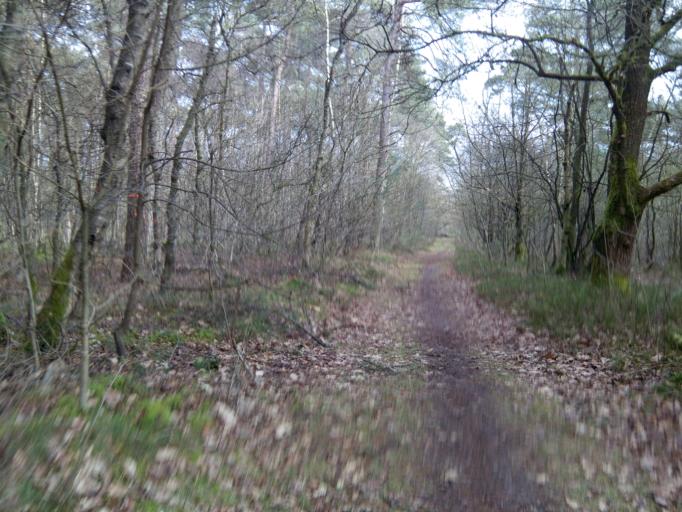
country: NL
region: Utrecht
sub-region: Gemeente Utrechtse Heuvelrug
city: Driebergen-Rijsenburg
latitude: 52.1080
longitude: 5.3089
